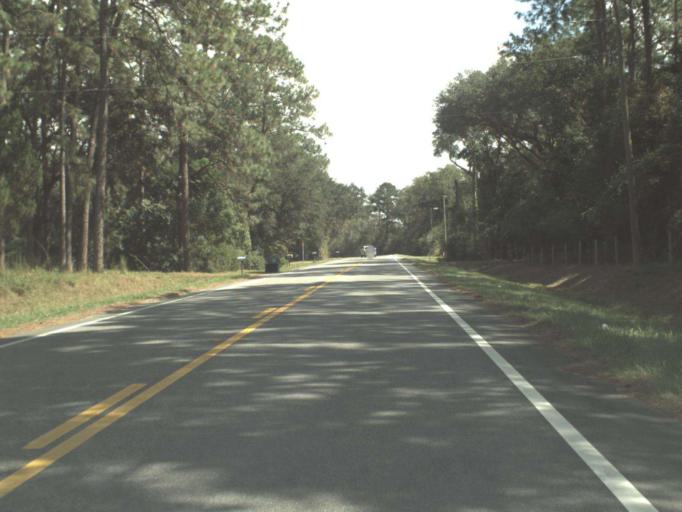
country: US
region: Florida
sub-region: Washington County
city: Chipley
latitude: 30.7899
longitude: -85.5350
